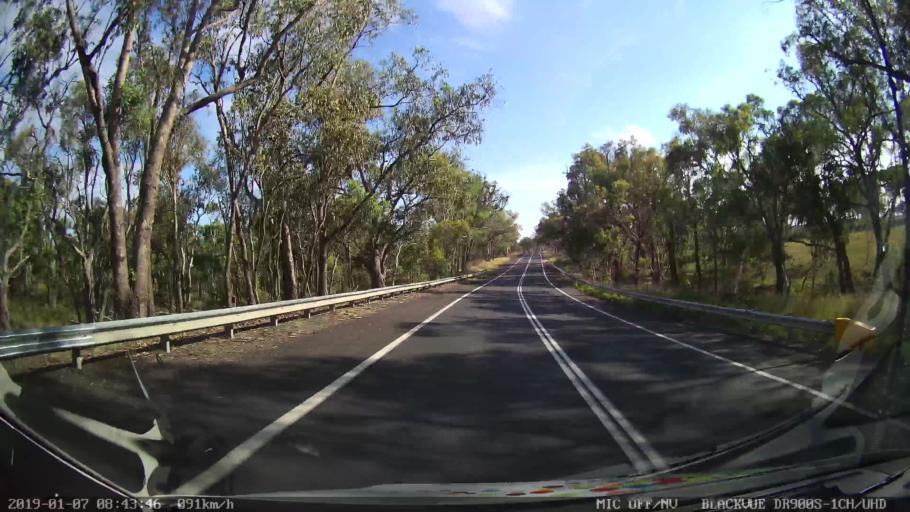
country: AU
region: New South Wales
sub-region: Tamworth Municipality
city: Kootingal
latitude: -30.8403
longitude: 151.2158
